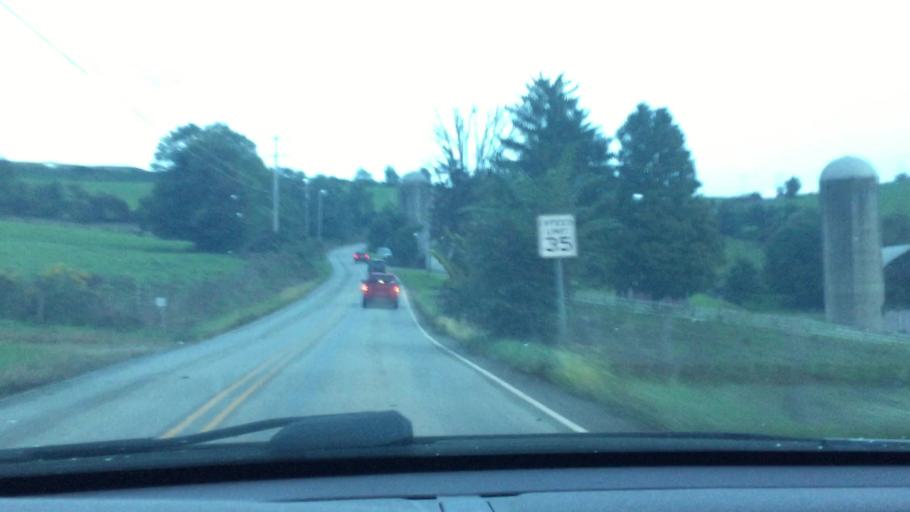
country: US
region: Pennsylvania
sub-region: Washington County
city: McGovern
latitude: 40.2012
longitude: -80.1981
